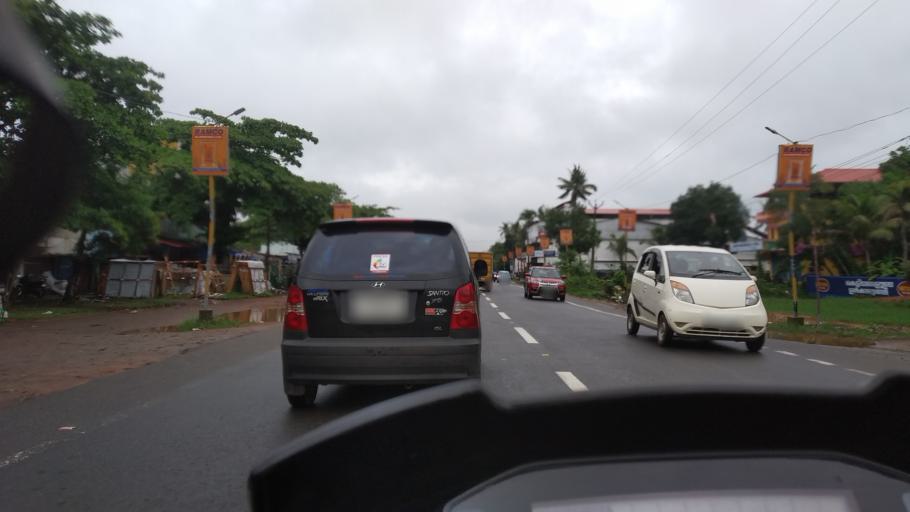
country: IN
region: Kerala
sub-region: Alappuzha
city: Mavelikara
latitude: 9.2814
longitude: 76.4508
